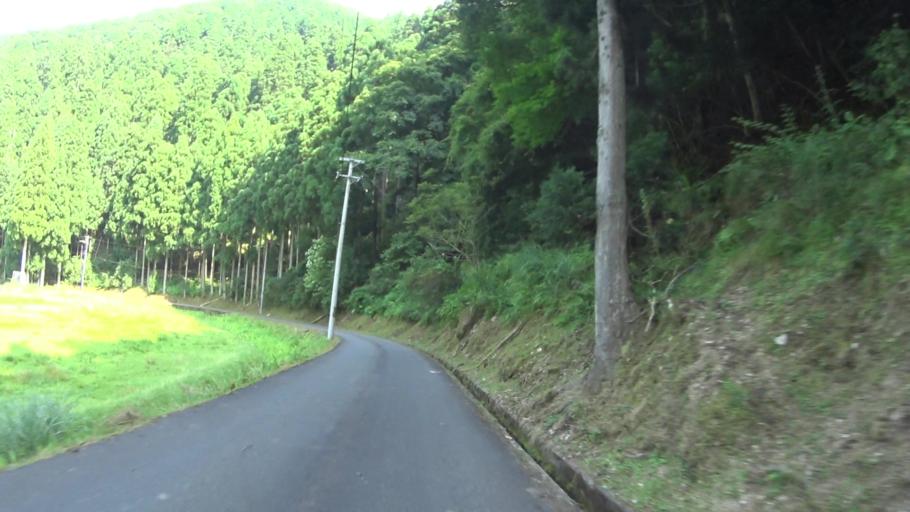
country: JP
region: Fukui
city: Obama
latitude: 35.2978
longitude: 135.6386
